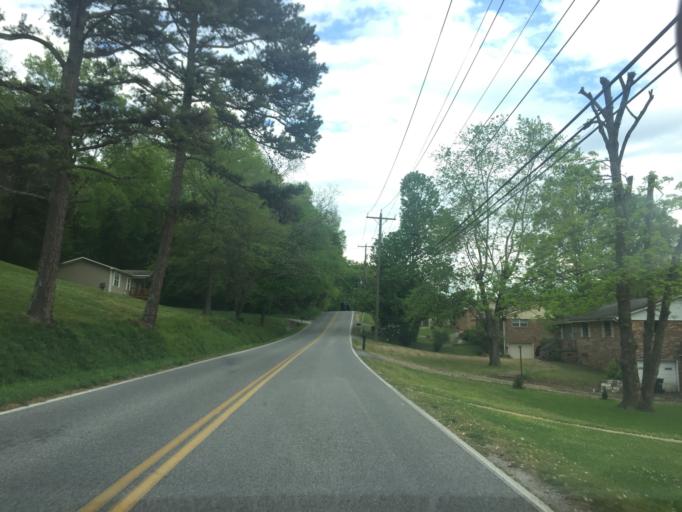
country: US
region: Tennessee
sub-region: Hamilton County
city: Harrison
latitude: 35.1225
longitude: -85.1217
